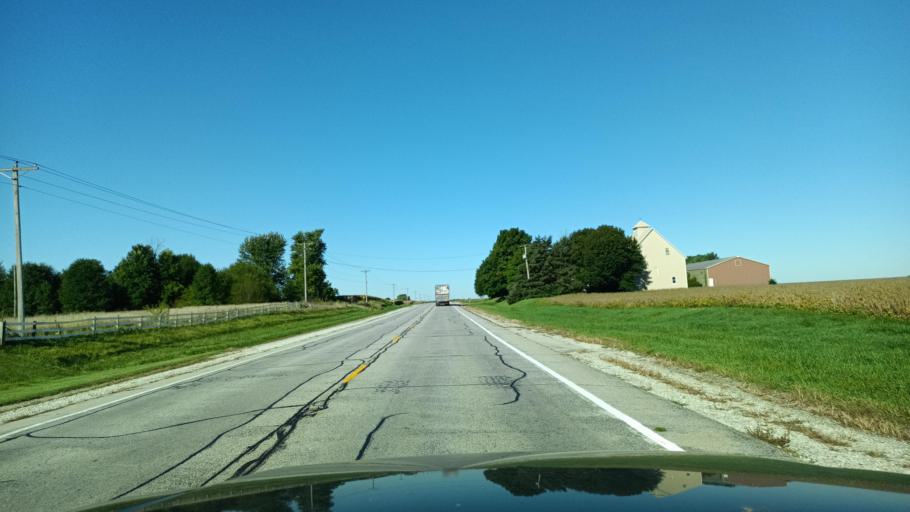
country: US
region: Illinois
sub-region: Warren County
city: Monmouth
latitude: 40.8785
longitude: -90.7107
